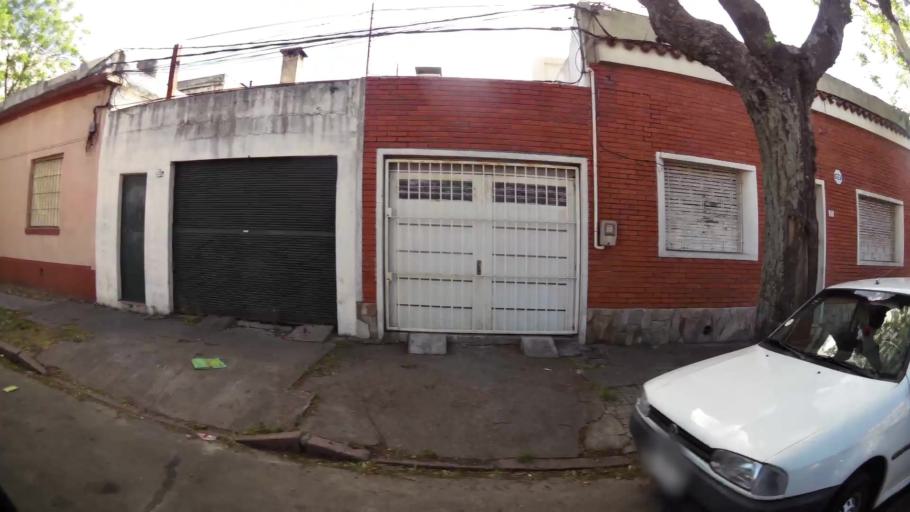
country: UY
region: Montevideo
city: Montevideo
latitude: -34.8762
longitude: -56.1488
